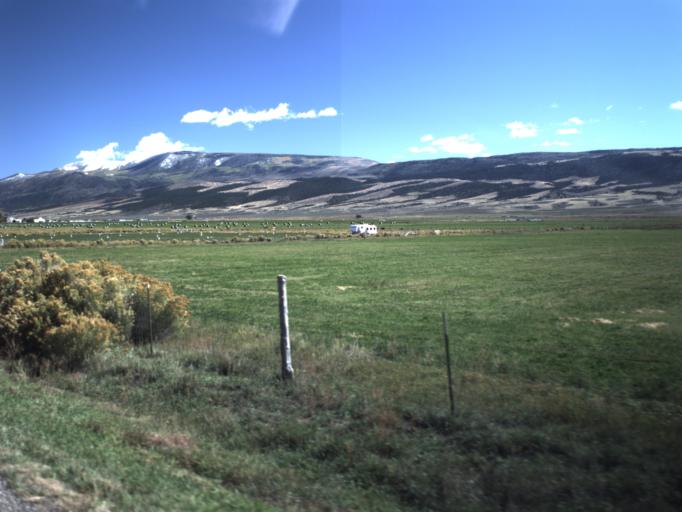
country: US
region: Utah
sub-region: Sevier County
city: Monroe
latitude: 38.4521
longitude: -111.9134
